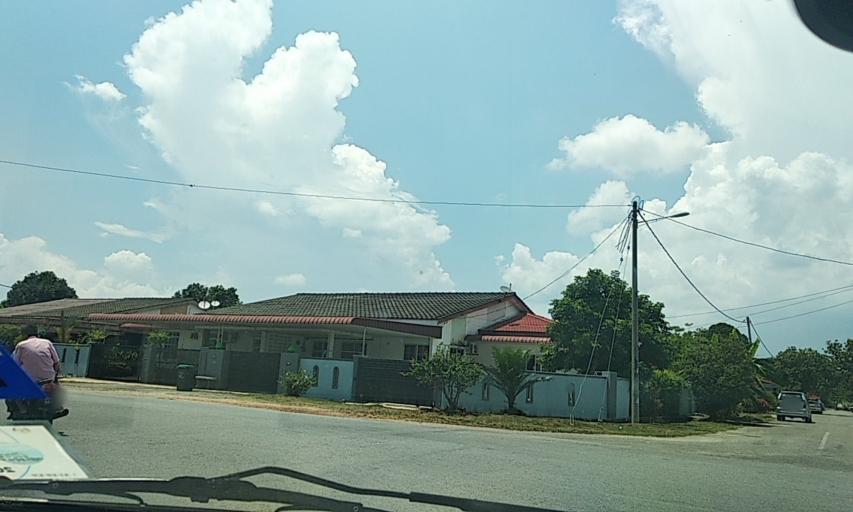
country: MY
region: Kedah
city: Sungai Petani
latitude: 5.6334
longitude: 100.4707
